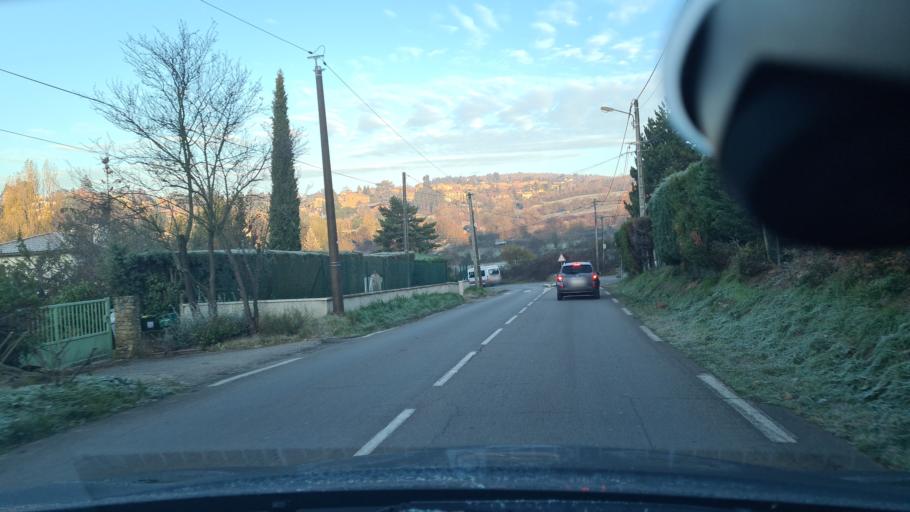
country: FR
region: Rhone-Alpes
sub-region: Departement du Rhone
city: Limonest
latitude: 45.8198
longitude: 4.8030
